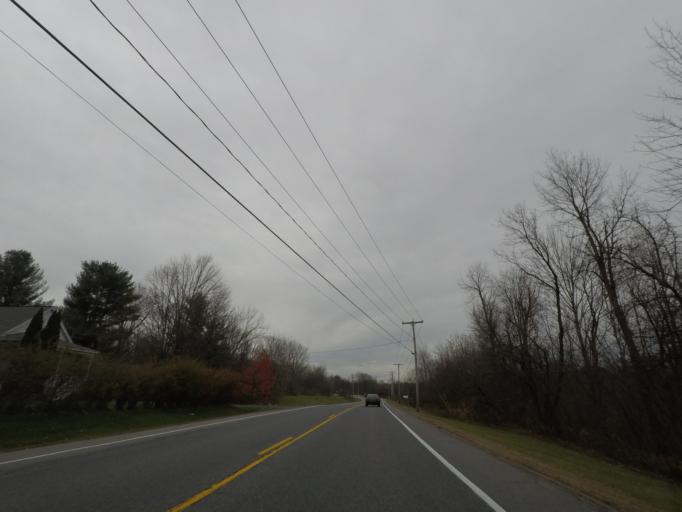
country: US
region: New York
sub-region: Saratoga County
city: Country Knolls
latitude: 42.8921
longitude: -73.8346
